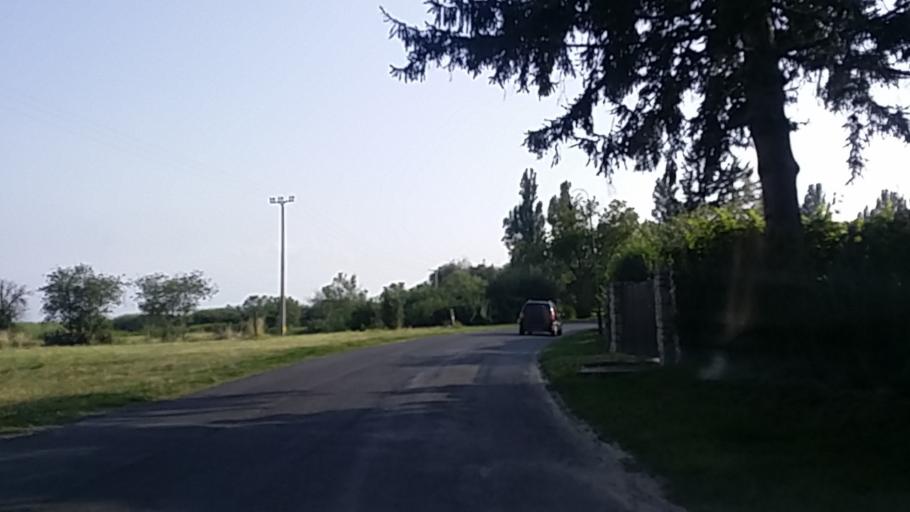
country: HU
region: Veszprem
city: Badacsonytomaj
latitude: 46.7873
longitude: 17.4483
